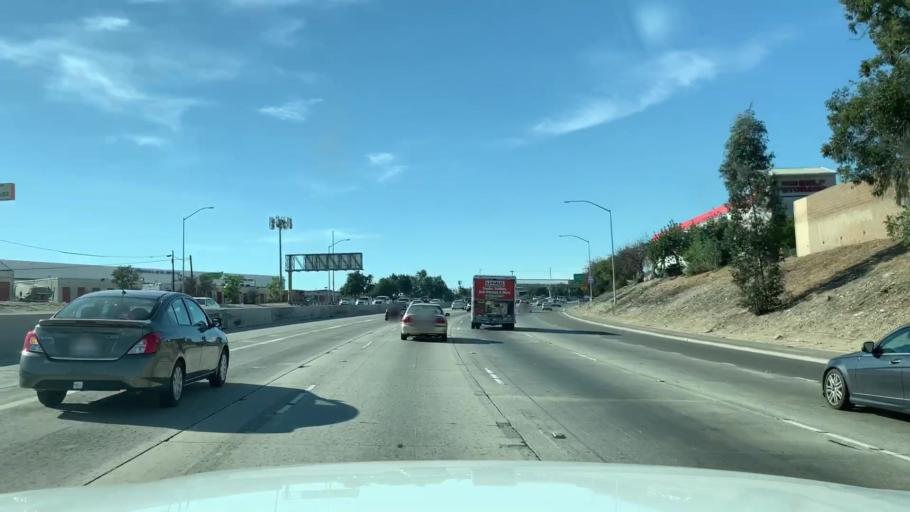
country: US
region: California
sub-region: Los Angeles County
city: North Hollywood
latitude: 34.2223
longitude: -118.3691
